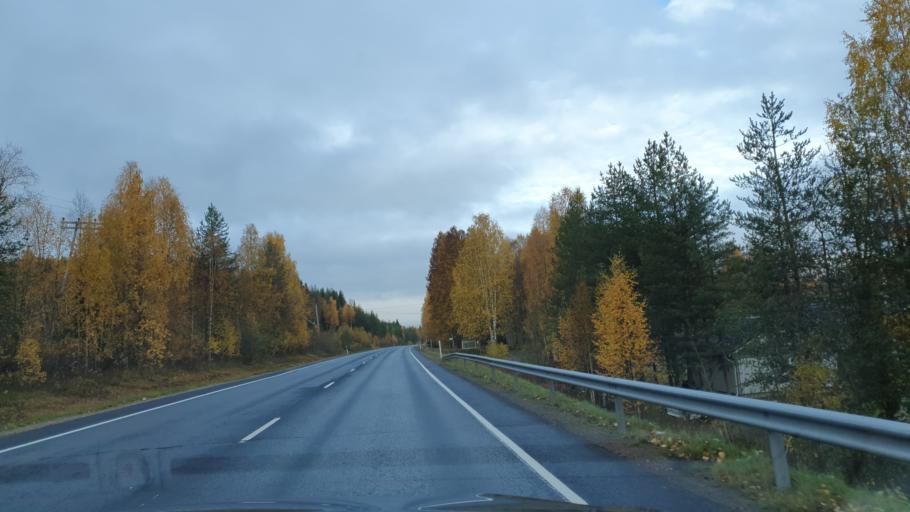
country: FI
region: Lapland
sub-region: Rovaniemi
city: Rovaniemi
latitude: 66.6037
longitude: 25.5817
